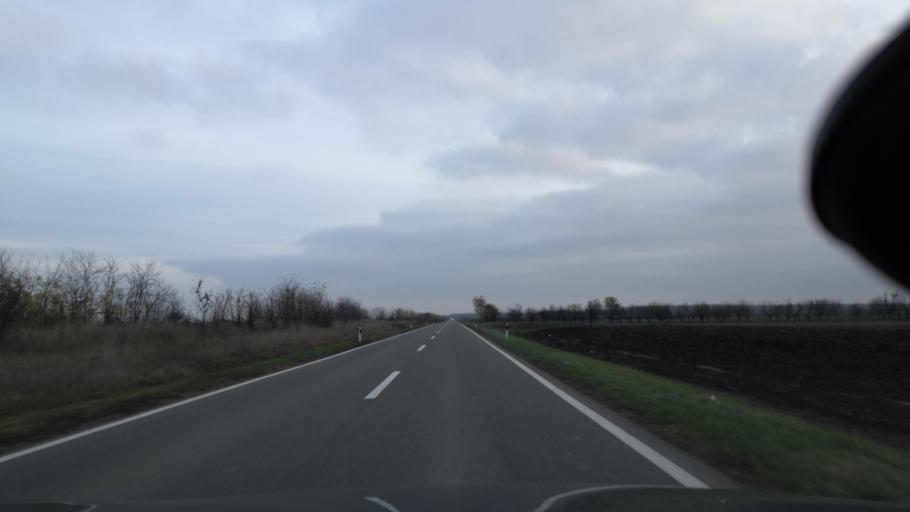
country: RS
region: Autonomna Pokrajina Vojvodina
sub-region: Severnobanatski Okrug
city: Novi Knezevac
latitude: 46.0139
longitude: 20.0979
